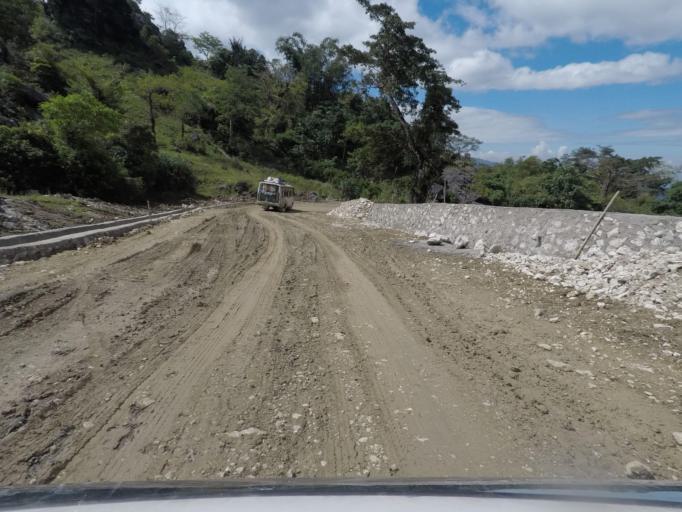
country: TL
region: Baucau
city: Venilale
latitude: -8.7308
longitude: 126.3683
